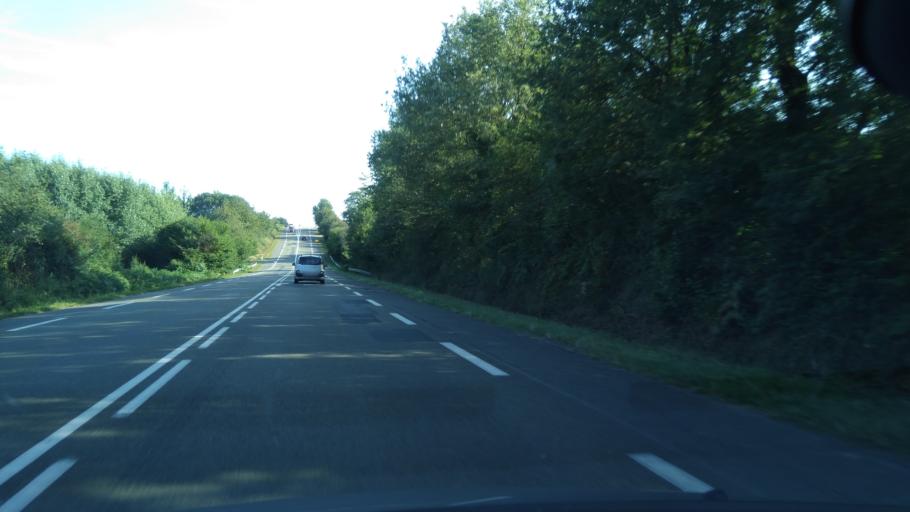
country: FR
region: Pays de la Loire
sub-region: Departement de la Mayenne
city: Entrammes
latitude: 47.9817
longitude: -0.7107
